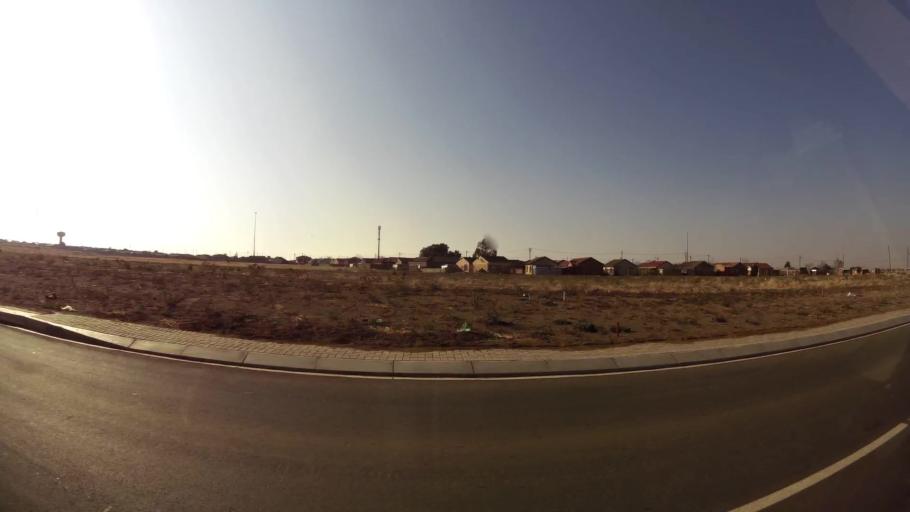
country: ZA
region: Orange Free State
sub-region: Mangaung Metropolitan Municipality
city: Bloemfontein
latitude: -29.1989
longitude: 26.2174
